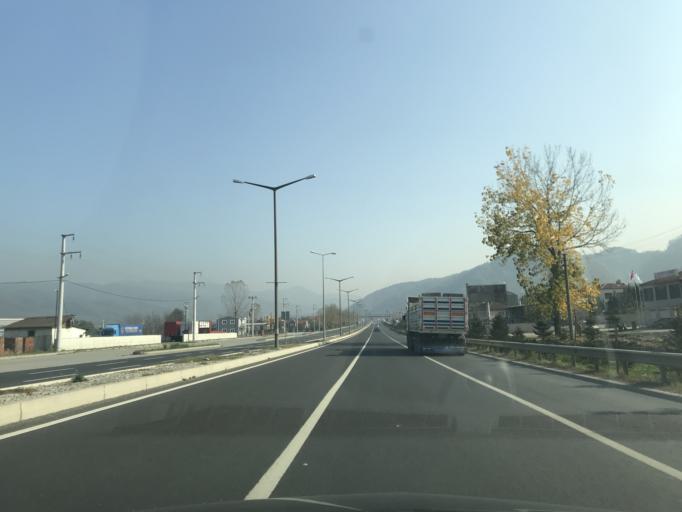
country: TR
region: Duzce
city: Kaynasli
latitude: 40.7754
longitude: 31.3080
